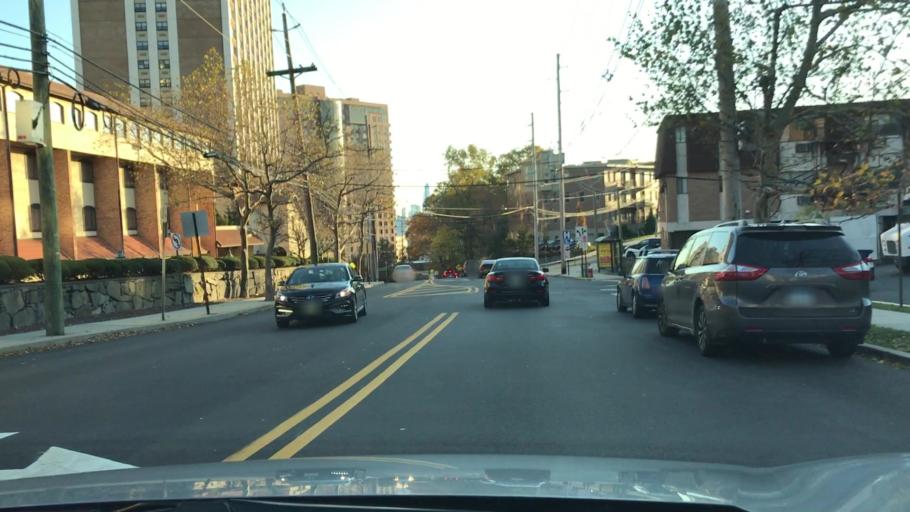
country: US
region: New Jersey
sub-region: Bergen County
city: Cliffside Park
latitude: 40.8139
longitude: -73.9901
